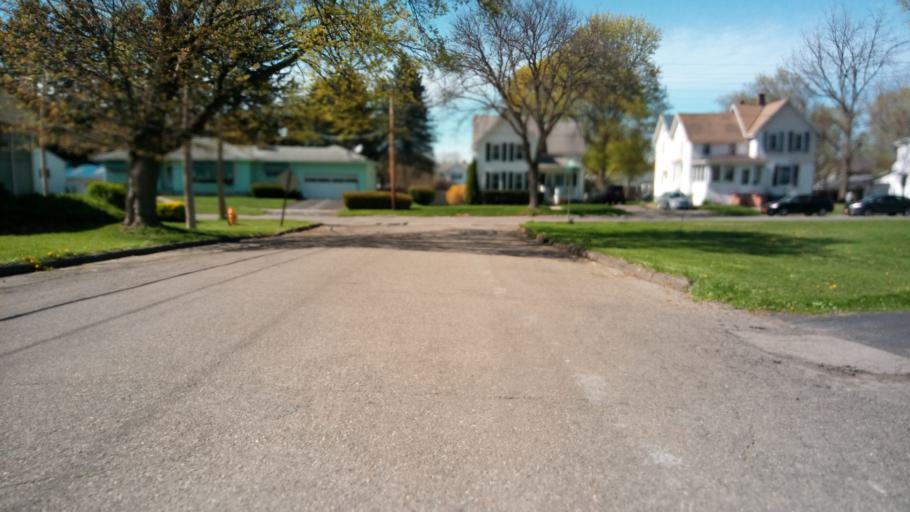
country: US
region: New York
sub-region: Chemung County
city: Elmira Heights
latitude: 42.1151
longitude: -76.8239
